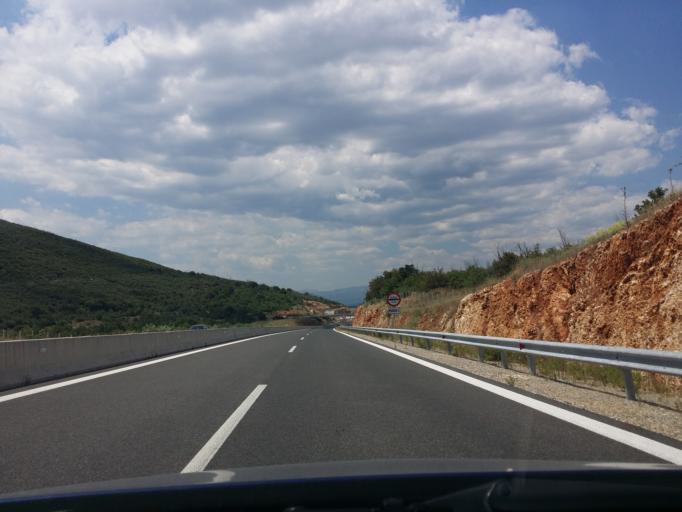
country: GR
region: Peloponnese
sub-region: Nomos Arkadias
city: Megalopoli
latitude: 37.2916
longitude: 22.2128
